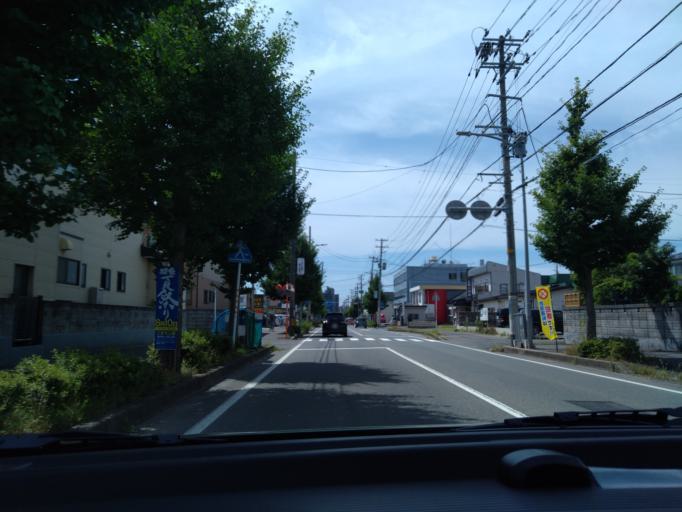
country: JP
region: Akita
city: Akita
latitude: 39.7123
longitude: 140.1367
